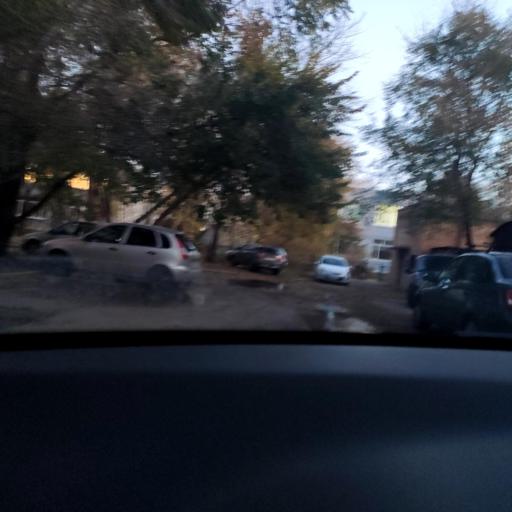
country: RU
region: Samara
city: Samara
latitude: 53.1978
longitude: 50.1762
